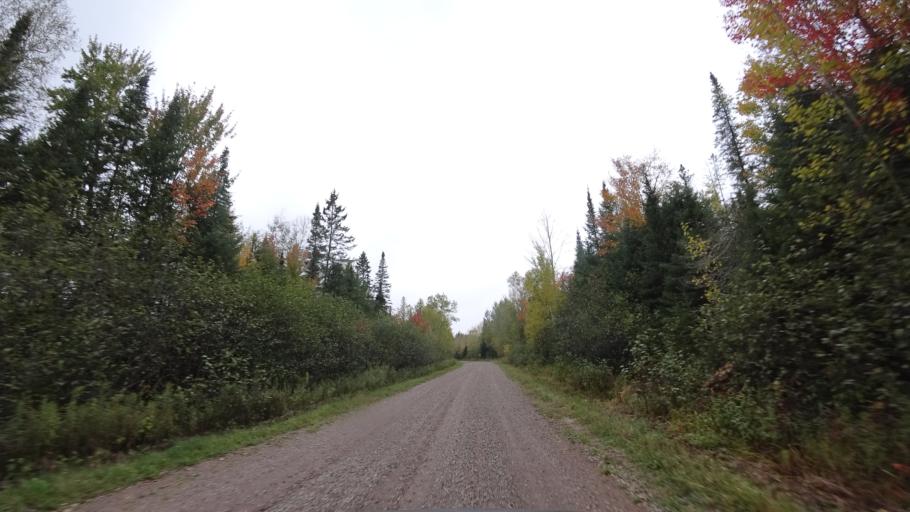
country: US
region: Wisconsin
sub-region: Sawyer County
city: Little Round Lake
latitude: 45.9753
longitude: -90.9902
